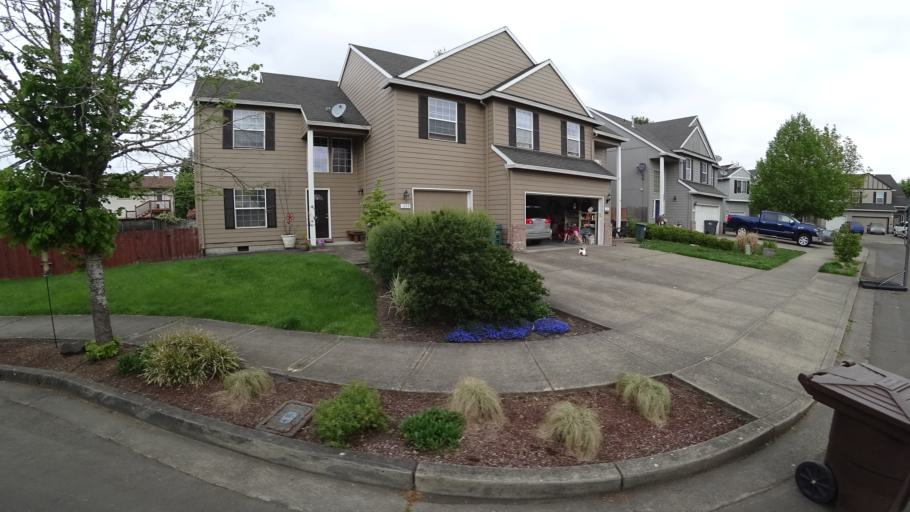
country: US
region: Oregon
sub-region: Washington County
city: Hillsboro
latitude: 45.5376
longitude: -122.9684
